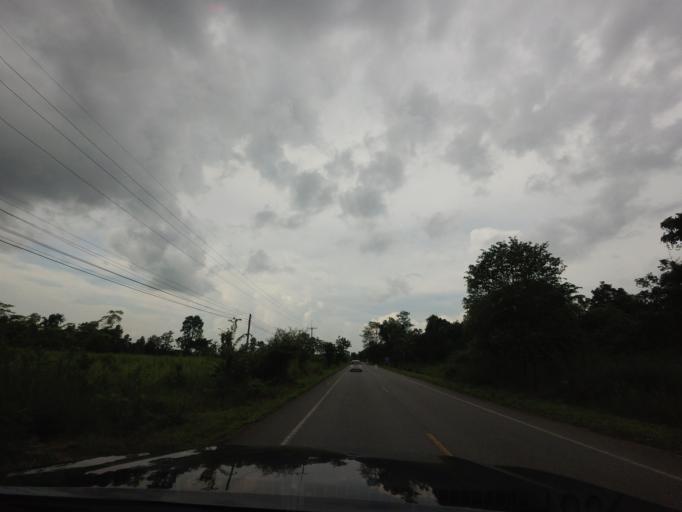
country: TH
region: Changwat Nong Bua Lamphu
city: Nong Bua Lamphu
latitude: 17.3040
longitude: 102.3858
